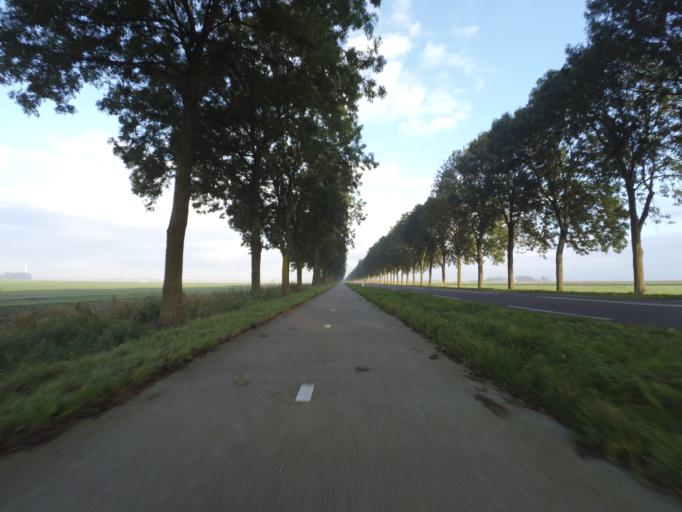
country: NL
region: Flevoland
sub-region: Gemeente Dronten
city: Biddinghuizen
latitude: 52.4664
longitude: 5.6849
